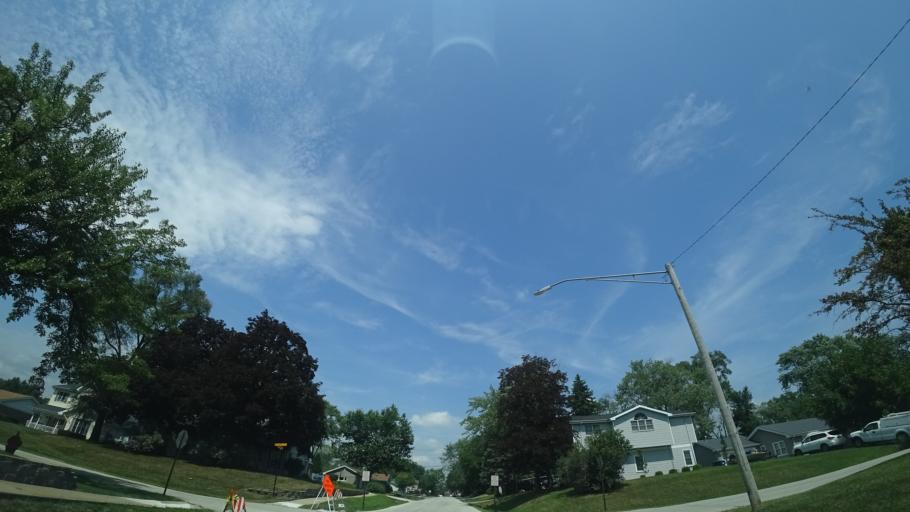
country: US
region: Illinois
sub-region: Cook County
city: Worth
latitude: 41.6852
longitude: -87.7914
